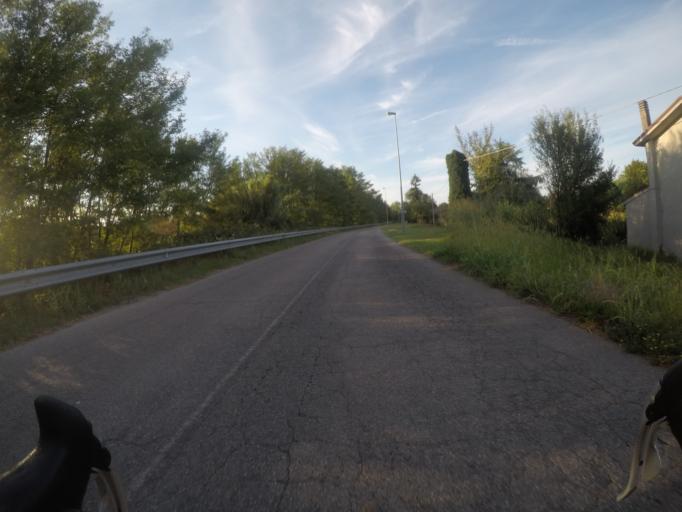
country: IT
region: Veneto
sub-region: Provincia di Rovigo
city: Castelguglielmo
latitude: 45.0061
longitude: 11.5633
